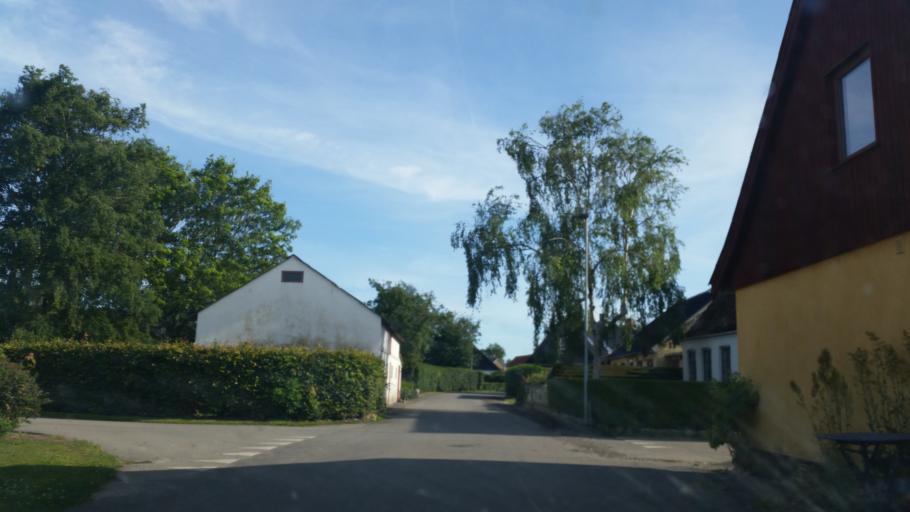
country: DK
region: Central Jutland
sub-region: Samso Kommune
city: Tranebjerg
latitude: 55.9640
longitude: 10.5556
